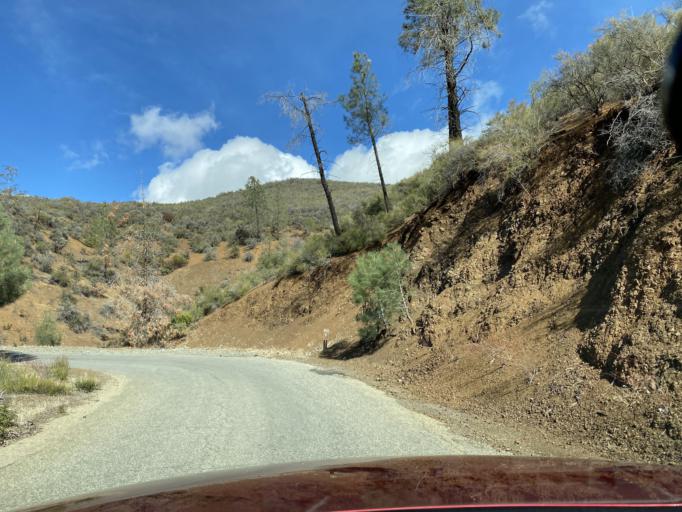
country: US
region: California
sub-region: Lake County
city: Lucerne
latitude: 39.3658
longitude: -122.6313
